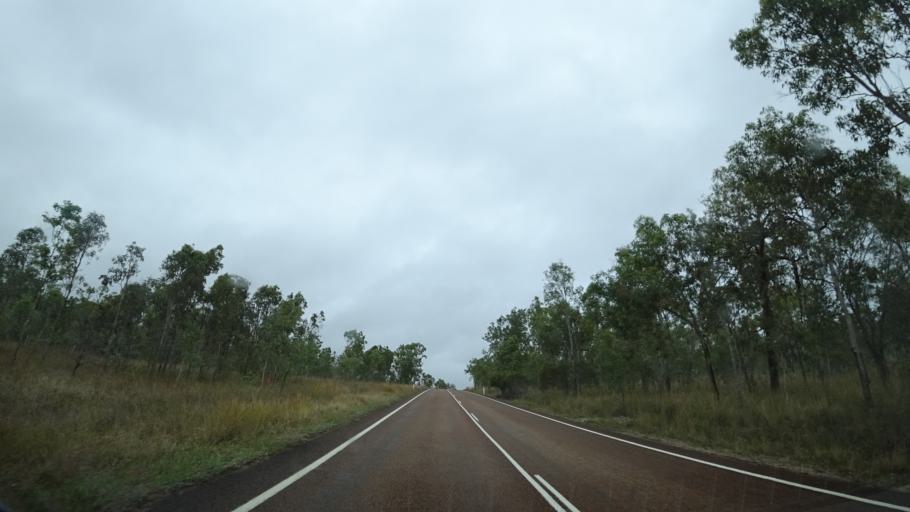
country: AU
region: Queensland
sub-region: Tablelands
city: Ravenshoe
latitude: -17.6823
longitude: 145.2332
